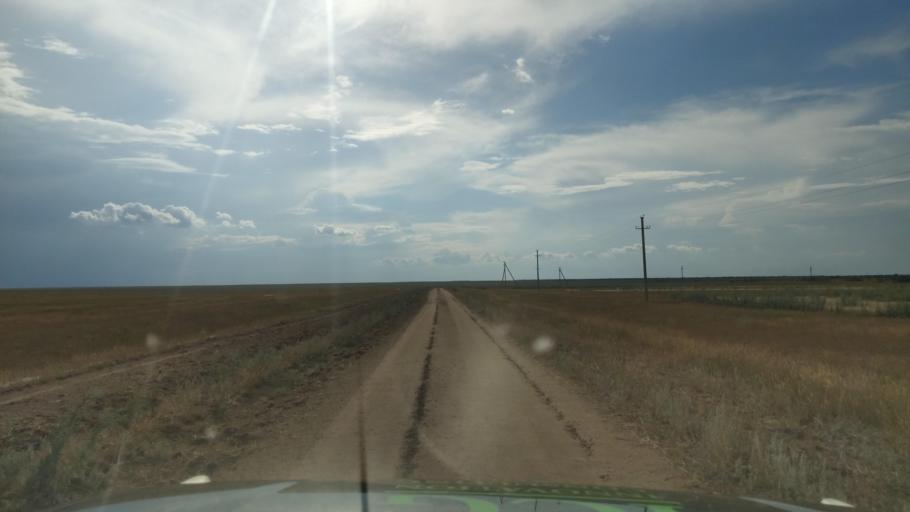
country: KZ
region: Pavlodar
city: Pavlodar
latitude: 52.5088
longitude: 77.5572
